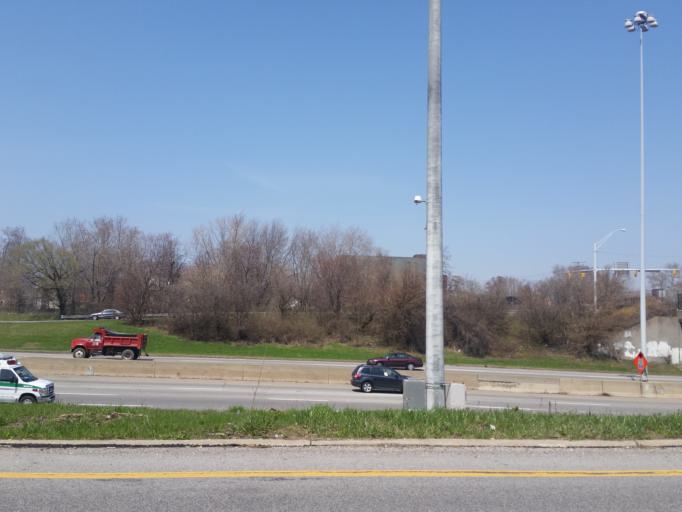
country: US
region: Ohio
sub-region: Cuyahoga County
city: Cleveland
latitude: 41.4747
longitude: -81.7171
